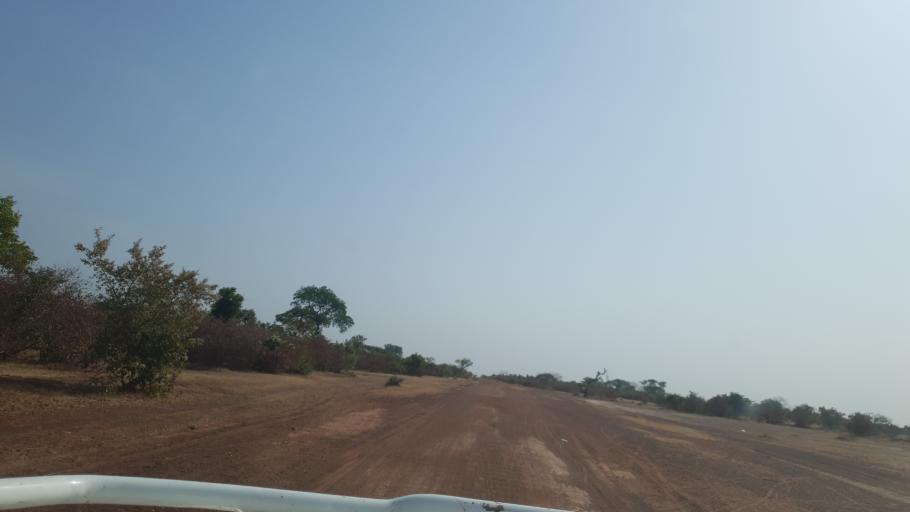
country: ML
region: Koulikoro
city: Dioila
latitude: 12.6694
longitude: -6.6670
